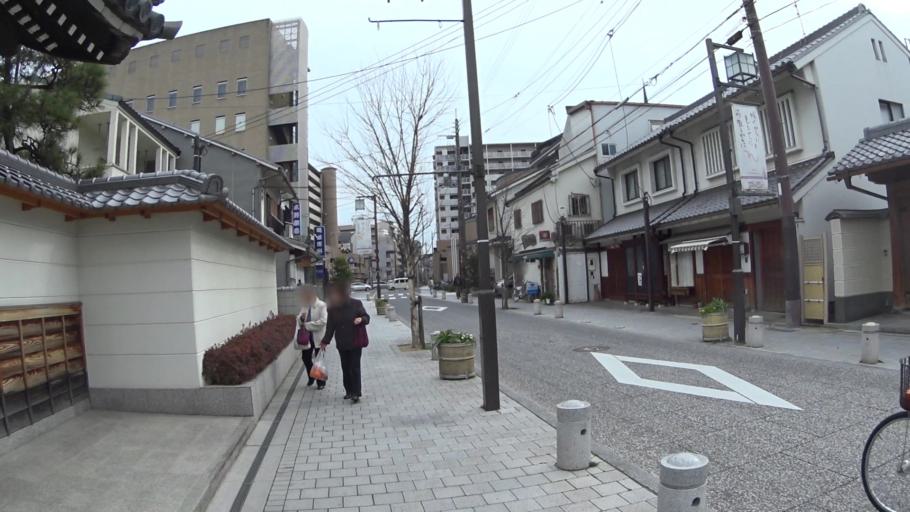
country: JP
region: Hyogo
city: Itami
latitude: 34.7806
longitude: 135.4157
